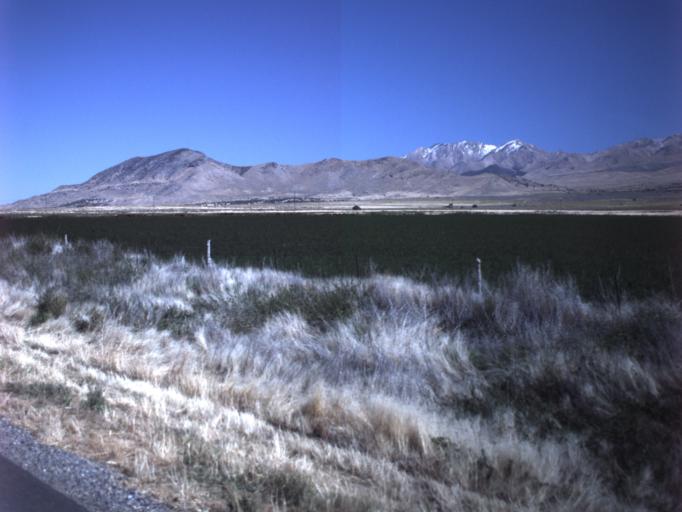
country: US
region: Utah
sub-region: Tooele County
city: Grantsville
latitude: 40.4988
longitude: -112.7480
